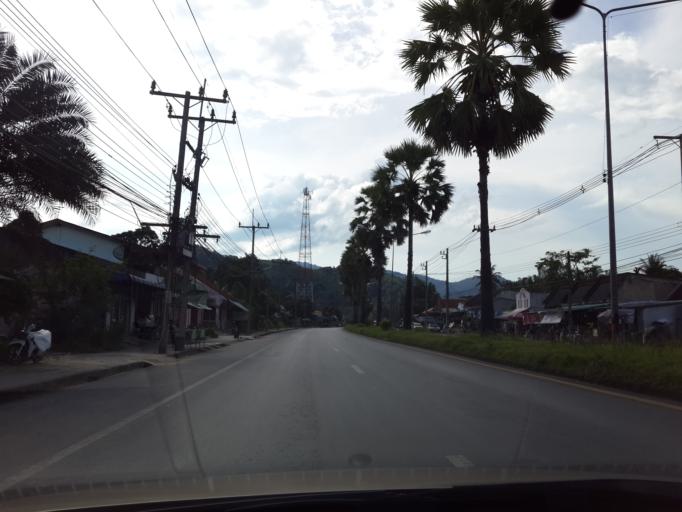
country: TH
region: Yala
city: Krong Pi Nang
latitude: 6.4579
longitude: 101.3388
